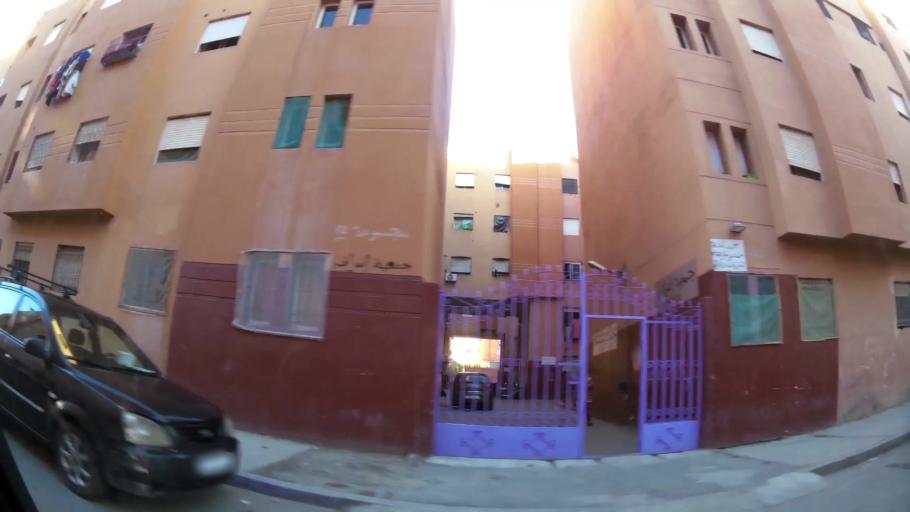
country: MA
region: Marrakech-Tensift-Al Haouz
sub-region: Marrakech
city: Marrakesh
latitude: 31.7496
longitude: -8.1184
